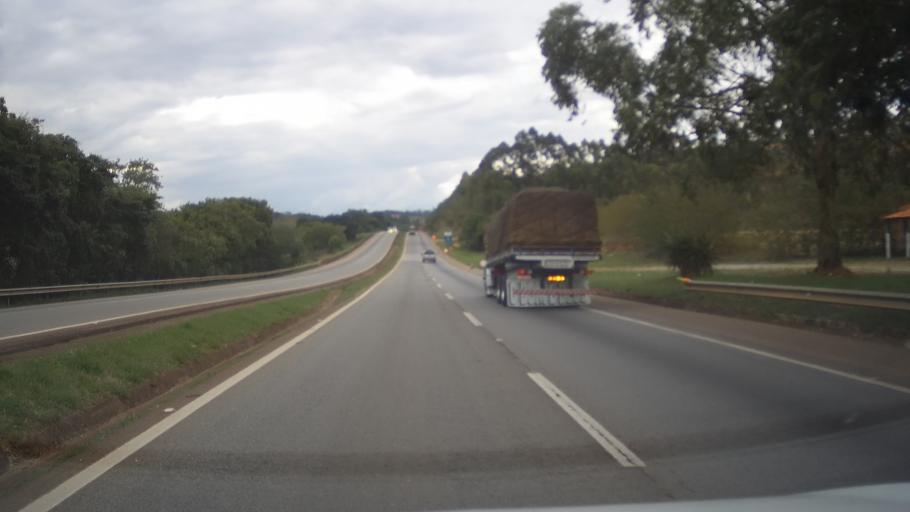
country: BR
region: Minas Gerais
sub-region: Itauna
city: Itauna
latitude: -20.3323
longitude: -44.4506
